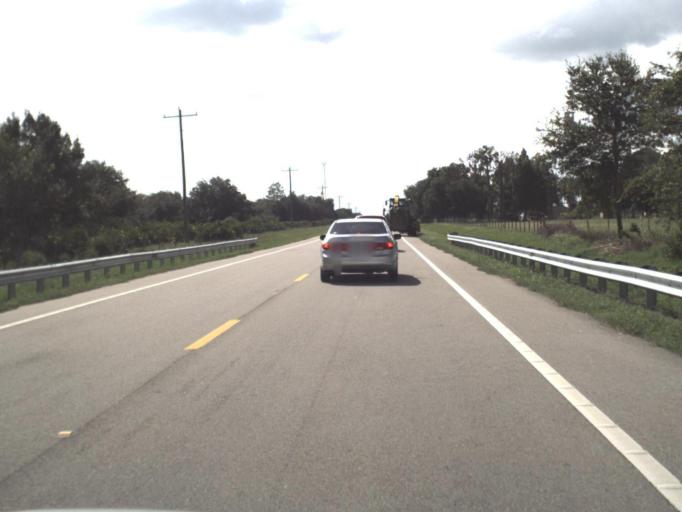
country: US
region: Florida
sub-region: Hillsborough County
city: Wimauma
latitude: 27.4738
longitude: -82.2346
